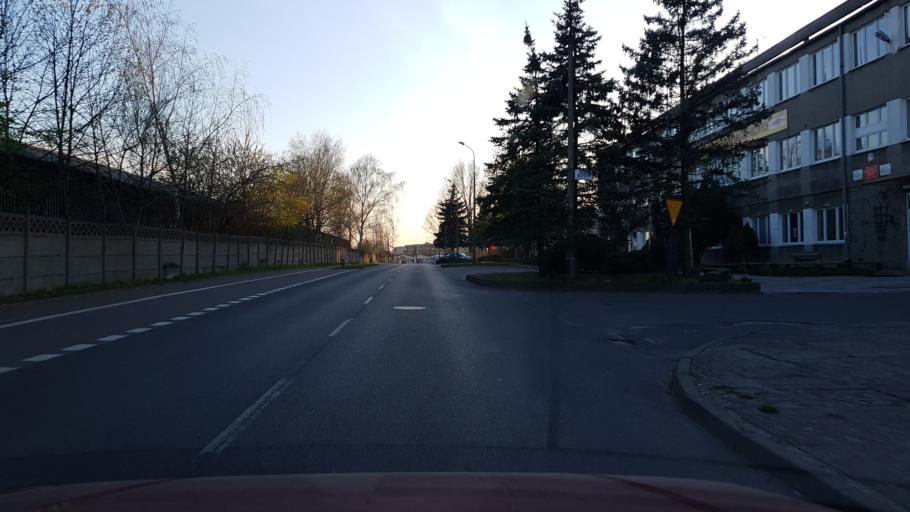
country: PL
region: West Pomeranian Voivodeship
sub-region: Powiat stargardzki
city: Stargard Szczecinski
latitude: 53.3479
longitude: 15.0158
